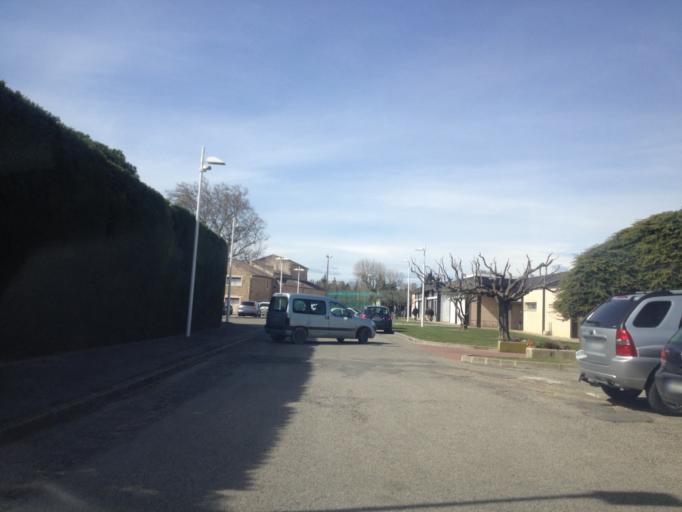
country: FR
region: Provence-Alpes-Cote d'Azur
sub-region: Departement du Vaucluse
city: Camaret-sur-Aigues
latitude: 44.1649
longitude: 4.8788
